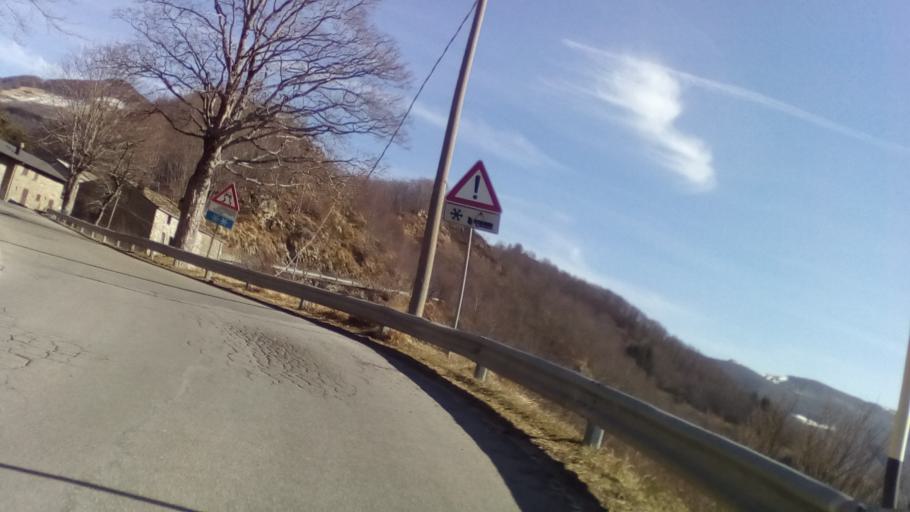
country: IT
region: Tuscany
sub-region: Provincia di Lucca
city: Castiglione di Garfagnana
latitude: 44.1786
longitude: 10.4625
